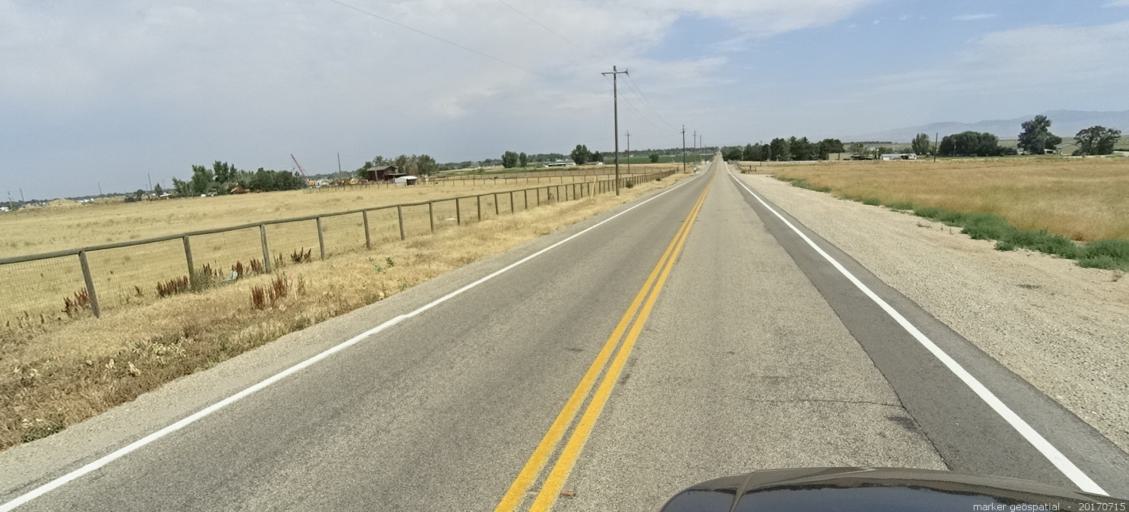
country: US
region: Idaho
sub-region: Ada County
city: Garden City
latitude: 43.5269
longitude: -116.2742
